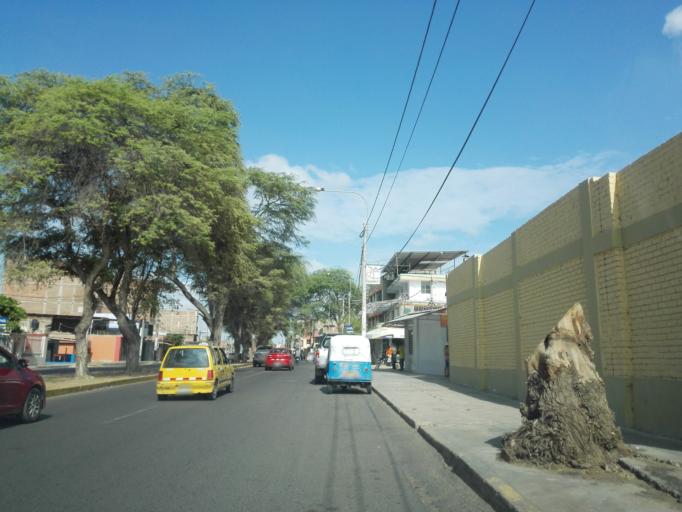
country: PE
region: Piura
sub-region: Provincia de Piura
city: Piura
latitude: -5.1884
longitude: -80.6502
